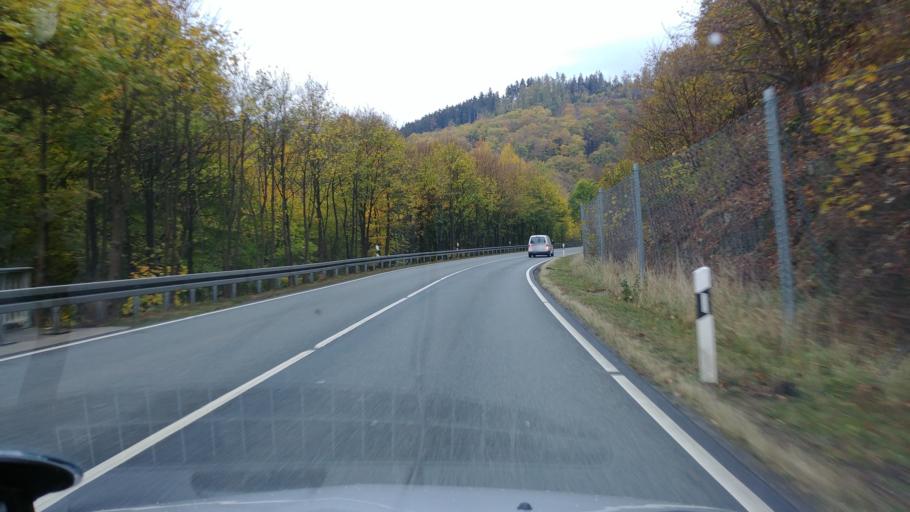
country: DE
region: Hesse
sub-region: Regierungsbezirk Darmstadt
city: Schlangenbad
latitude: 50.0987
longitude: 8.1048
